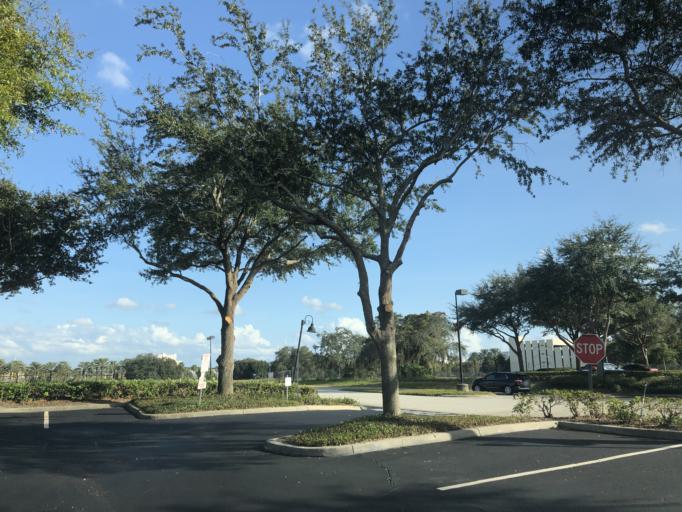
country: US
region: Florida
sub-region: Orange County
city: Doctor Phillips
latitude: 28.4356
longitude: -81.4710
